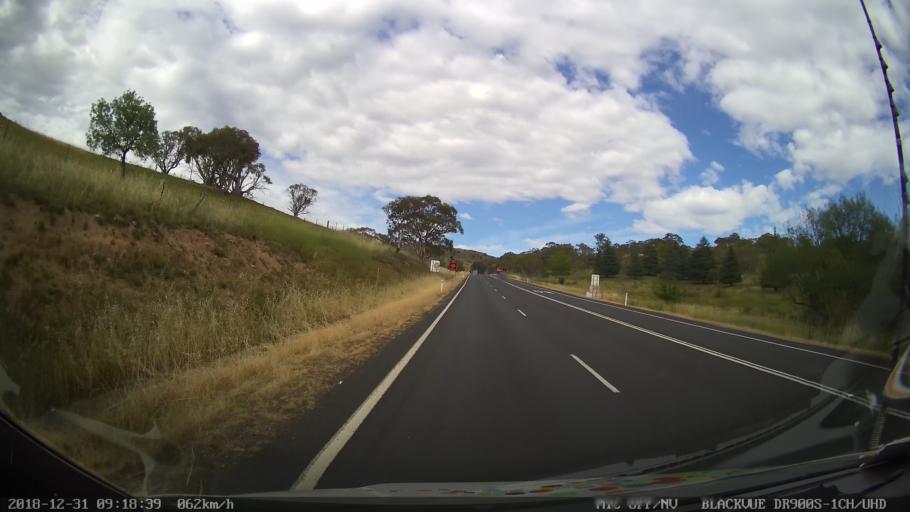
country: AU
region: New South Wales
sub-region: Snowy River
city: Jindabyne
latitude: -36.4104
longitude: 148.5922
